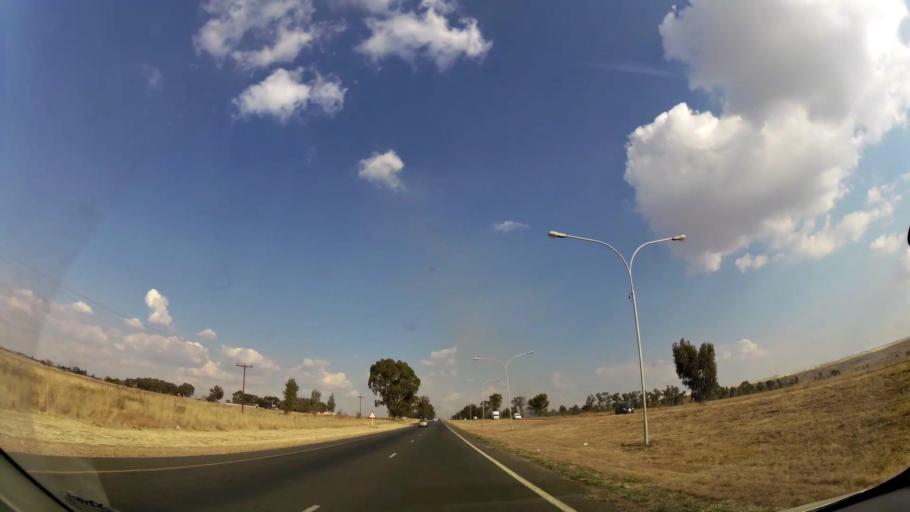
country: ZA
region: Gauteng
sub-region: Ekurhuleni Metropolitan Municipality
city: Brakpan
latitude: -26.3247
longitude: 28.3388
